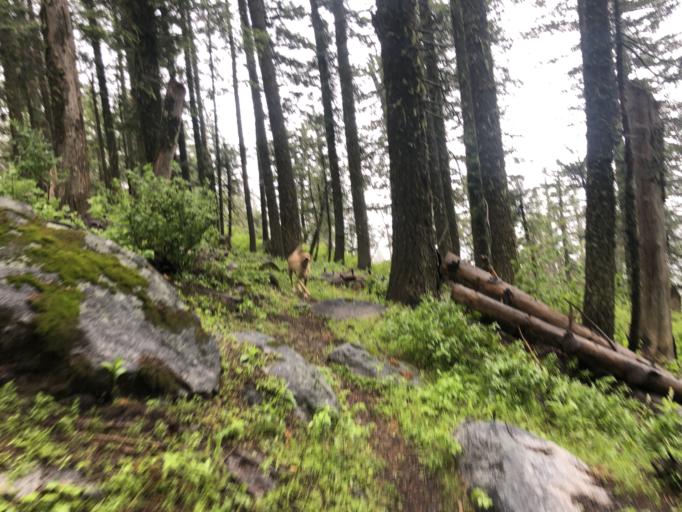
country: US
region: Idaho
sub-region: Latah County
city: Moscow
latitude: 46.8058
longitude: -116.8416
